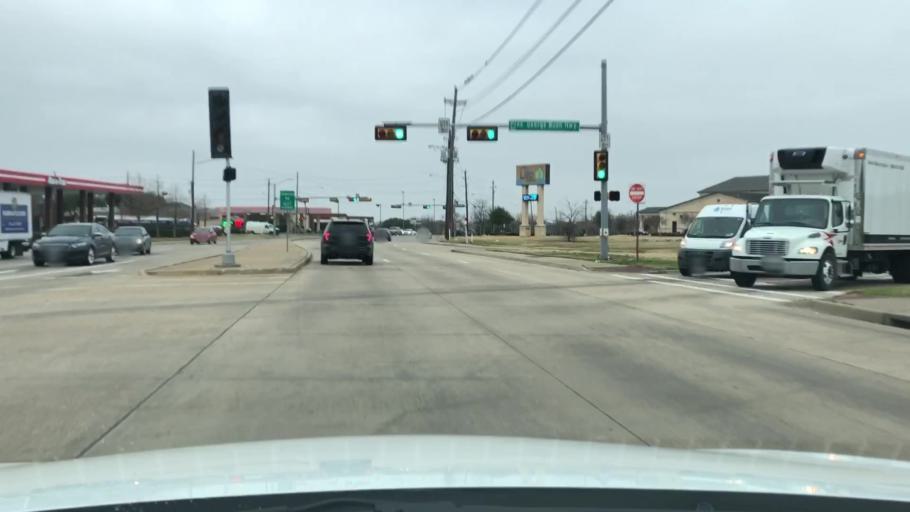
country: US
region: Texas
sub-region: Dallas County
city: Addison
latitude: 33.0020
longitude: -96.8567
